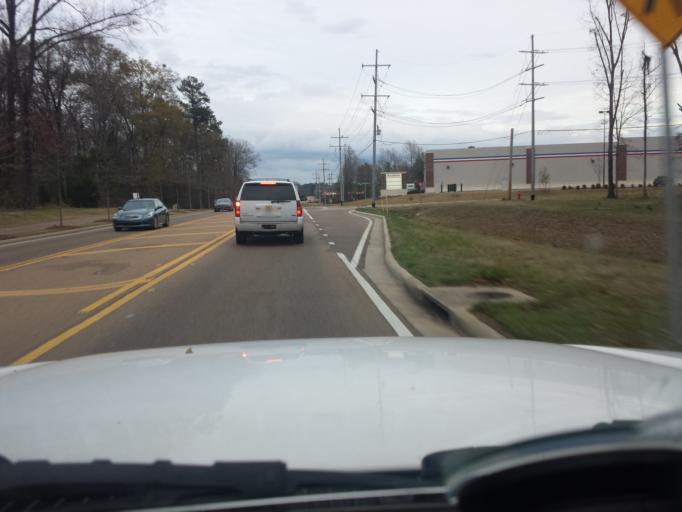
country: US
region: Mississippi
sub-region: Rankin County
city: Flowood
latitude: 32.3442
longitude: -90.0683
